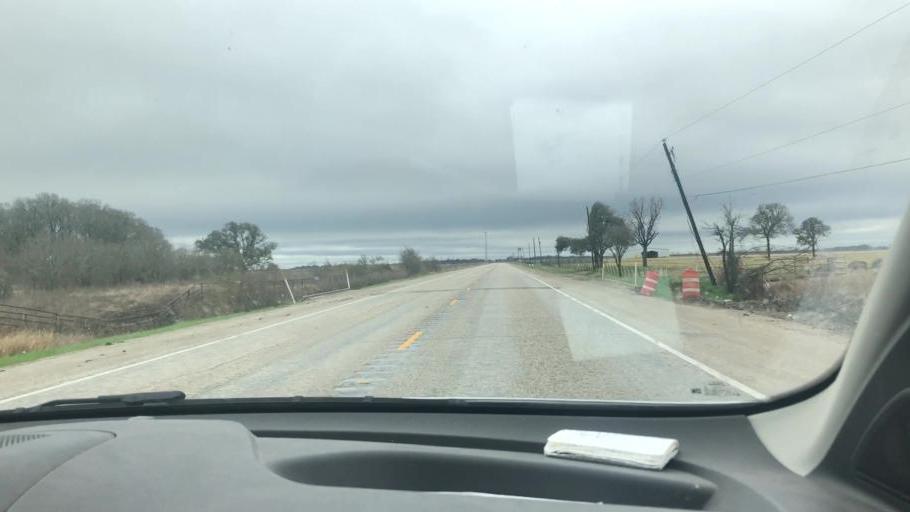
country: US
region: Texas
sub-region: Wharton County
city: Wharton
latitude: 29.2455
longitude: -96.0450
